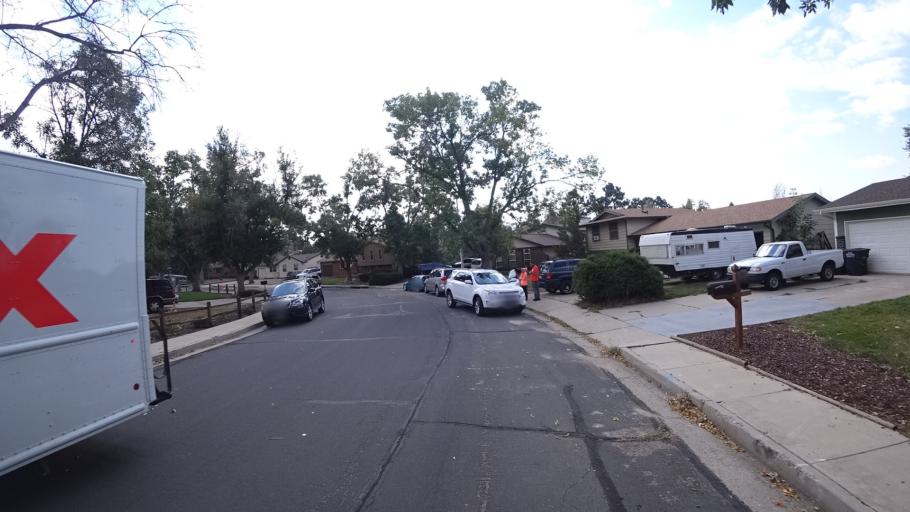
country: US
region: Colorado
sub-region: El Paso County
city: Cimarron Hills
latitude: 38.8798
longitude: -104.7436
